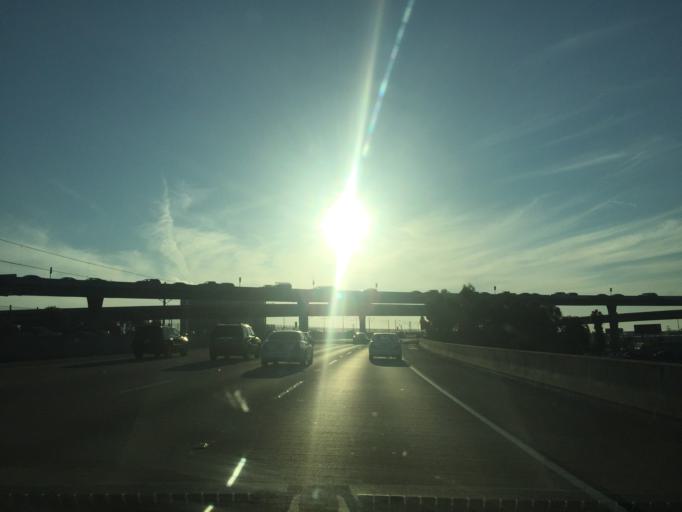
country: US
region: California
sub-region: Los Angeles County
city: Del Aire
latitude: 33.9307
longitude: -118.3664
